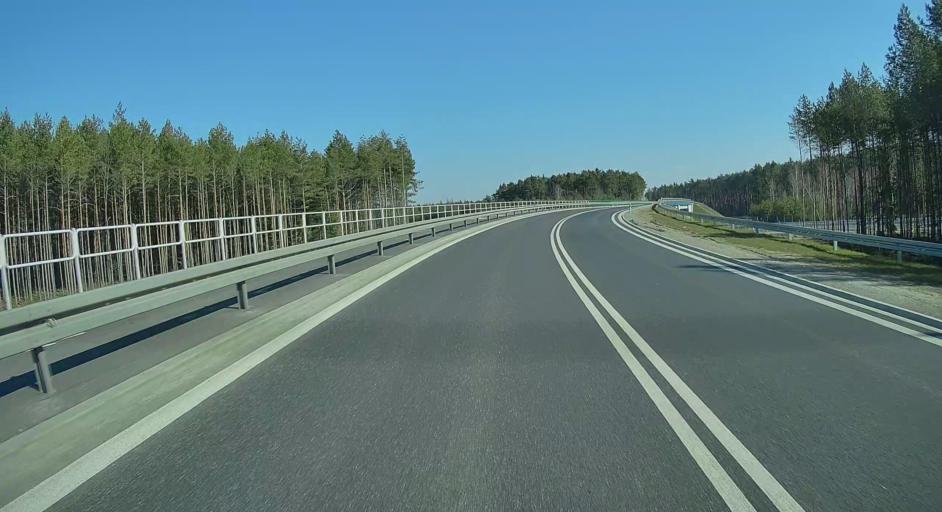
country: PL
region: Subcarpathian Voivodeship
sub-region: Powiat nizanski
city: Zarzecze
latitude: 50.5648
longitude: 22.2455
